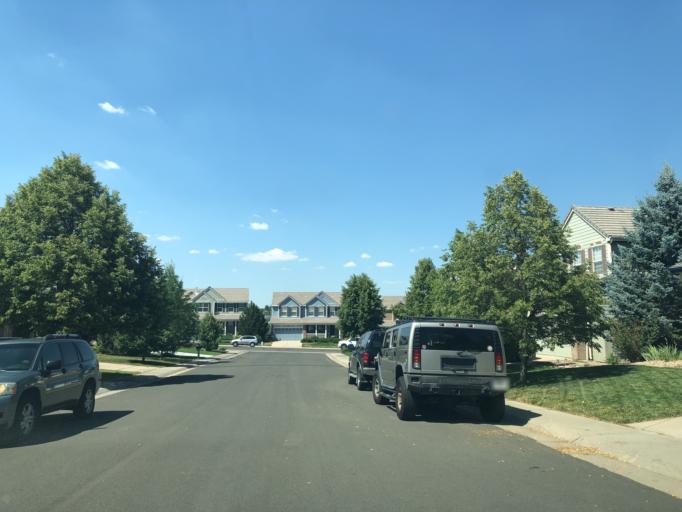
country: US
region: Colorado
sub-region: Arapahoe County
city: Dove Valley
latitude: 39.6042
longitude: -104.7785
